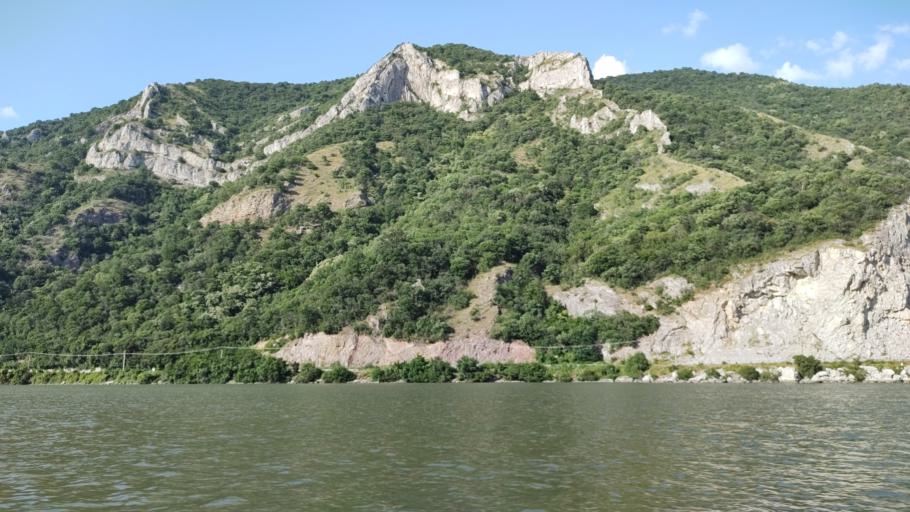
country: RO
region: Caras-Severin
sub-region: Comuna Berzasca
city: Berzasca
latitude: 44.6009
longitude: 22.0158
